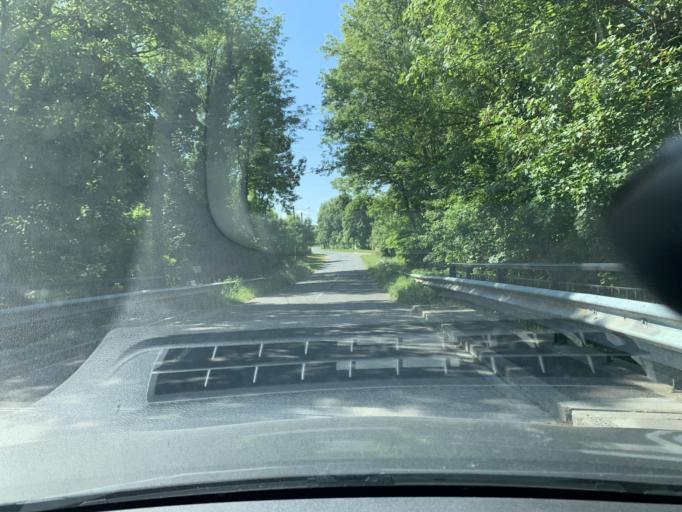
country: FR
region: Nord-Pas-de-Calais
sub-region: Departement du Pas-de-Calais
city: Oisy-le-Verger
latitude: 50.2624
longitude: 3.1405
